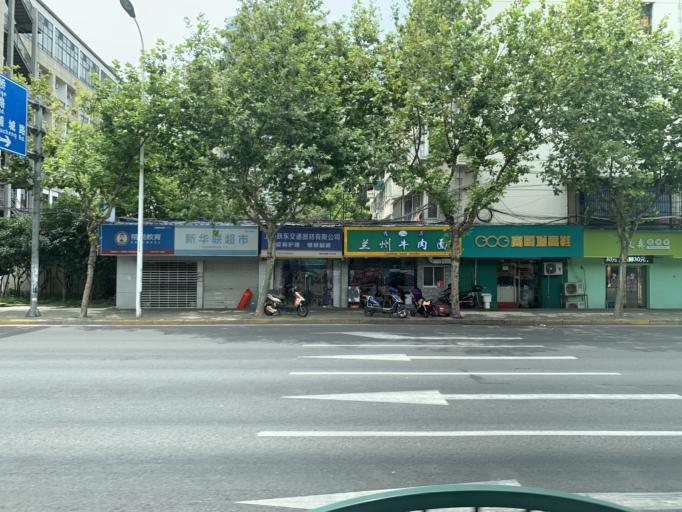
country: CN
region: Shanghai Shi
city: Pudong
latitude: 31.2257
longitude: 121.5130
